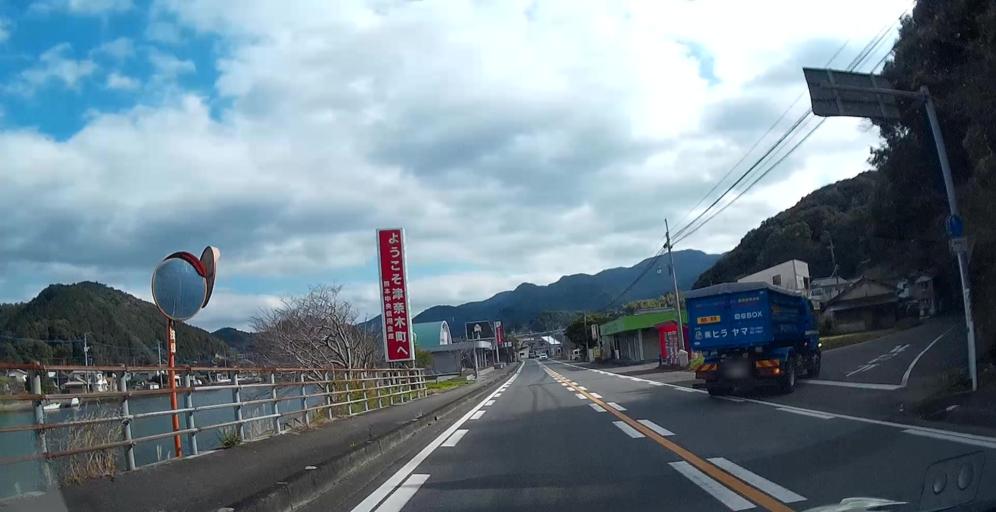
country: JP
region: Kumamoto
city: Minamata
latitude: 32.2342
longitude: 130.4455
